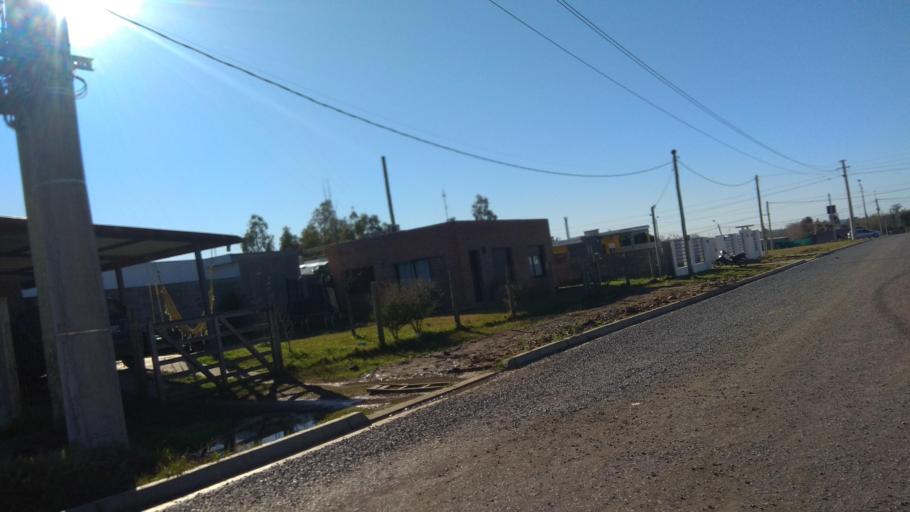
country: UY
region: Florida
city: Florida
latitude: -34.0880
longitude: -56.2391
